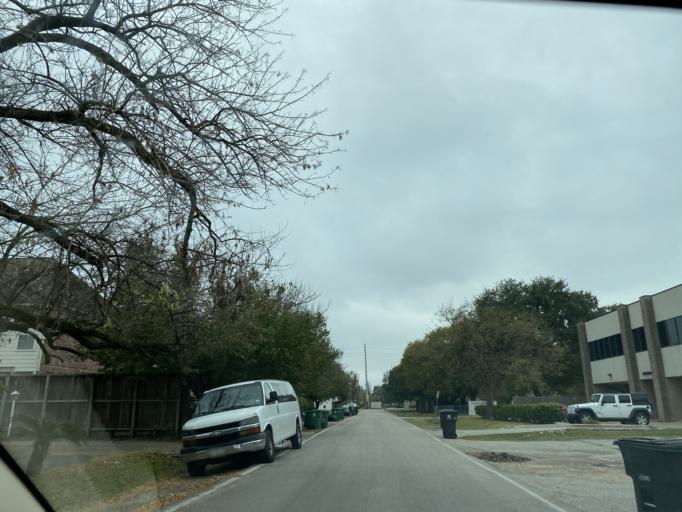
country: US
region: Texas
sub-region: Harris County
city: Bellaire
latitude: 29.7343
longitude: -95.4823
